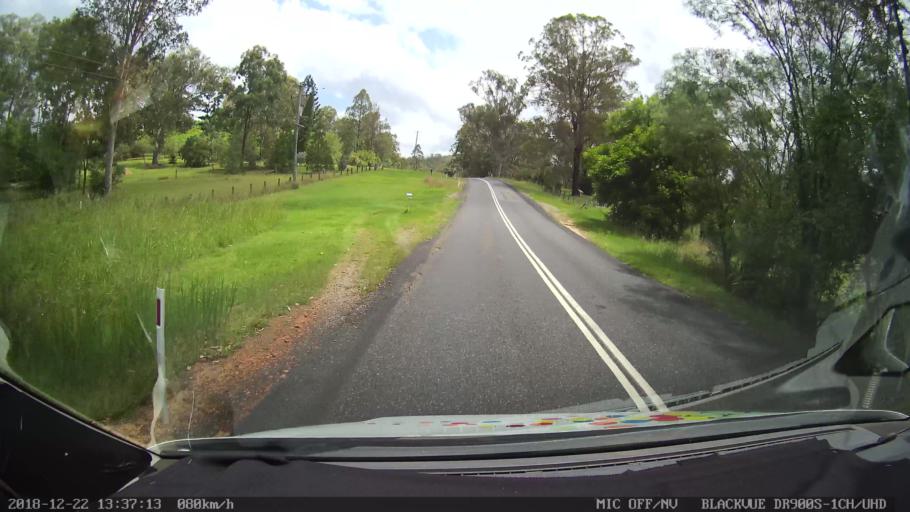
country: AU
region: New South Wales
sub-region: Clarence Valley
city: Coutts Crossing
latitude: -29.8877
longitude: 152.7887
